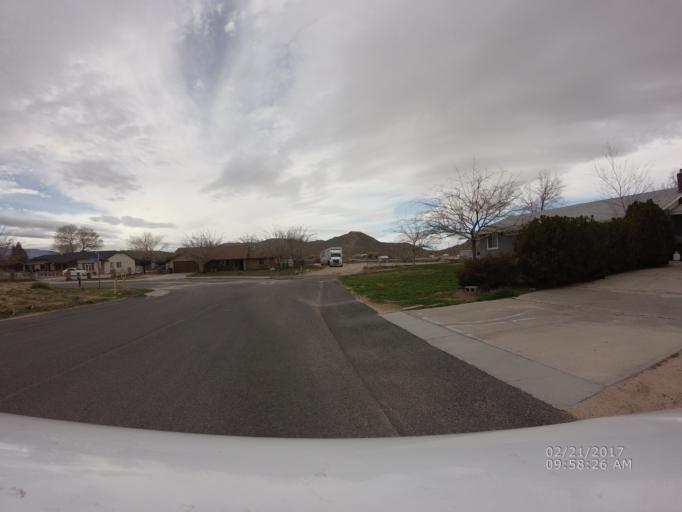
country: US
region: California
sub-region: Los Angeles County
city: Lake Los Angeles
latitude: 34.6059
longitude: -117.8227
